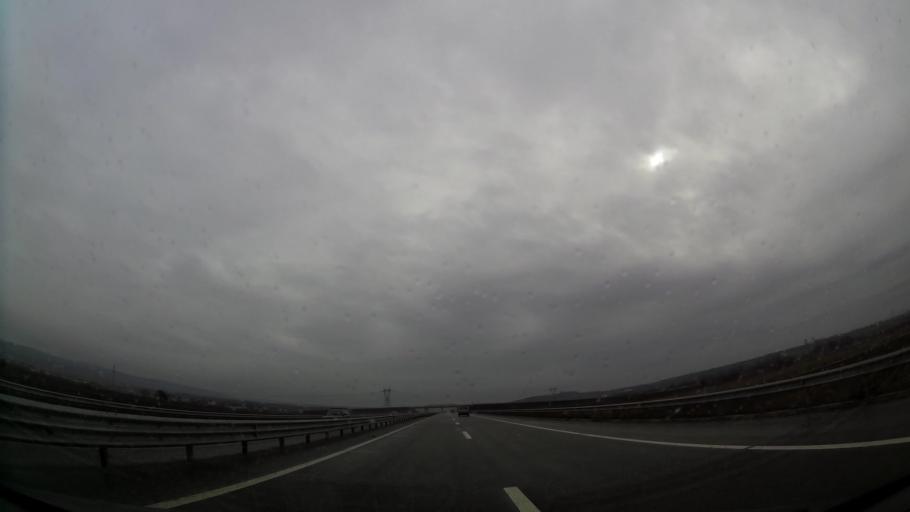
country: XK
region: Pristina
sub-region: Lipjan
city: Lipljan
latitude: 42.4548
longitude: 21.1835
